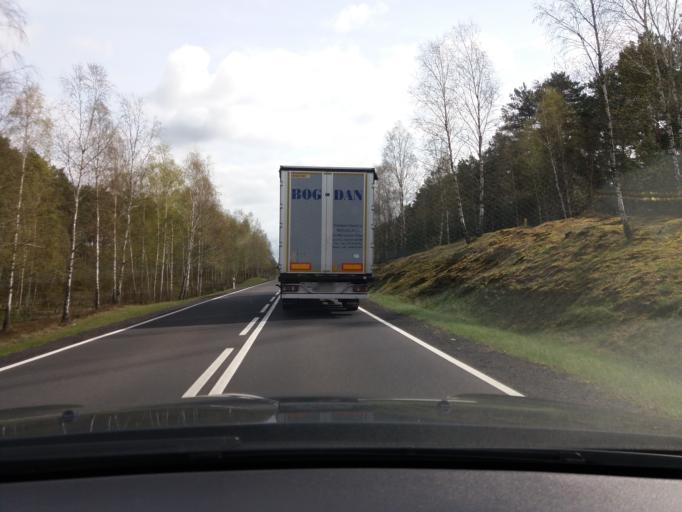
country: PL
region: Lubusz
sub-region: Powiat miedzyrzecki
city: Bledzew
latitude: 52.5913
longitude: 15.3665
